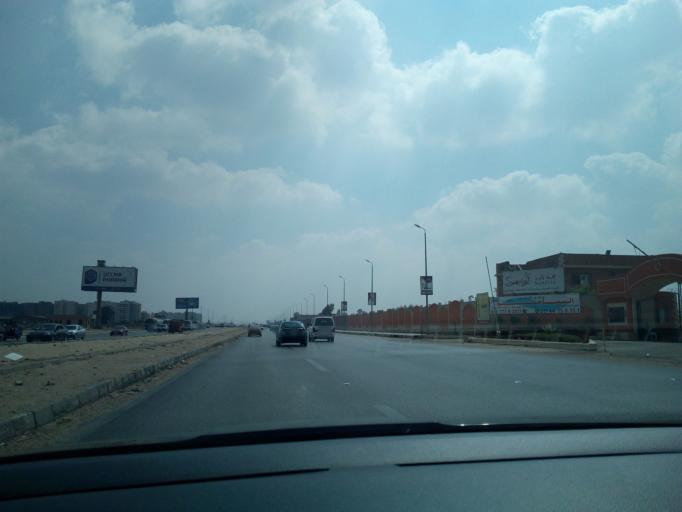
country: EG
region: Muhafazat al Qalyubiyah
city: Al Khankah
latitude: 30.1528
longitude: 31.4385
